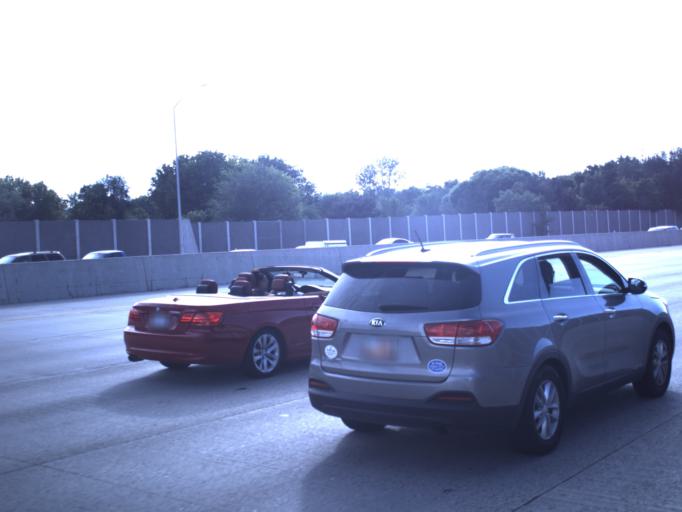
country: US
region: Utah
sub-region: Salt Lake County
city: Taylorsville
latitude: 40.6457
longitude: -111.9457
